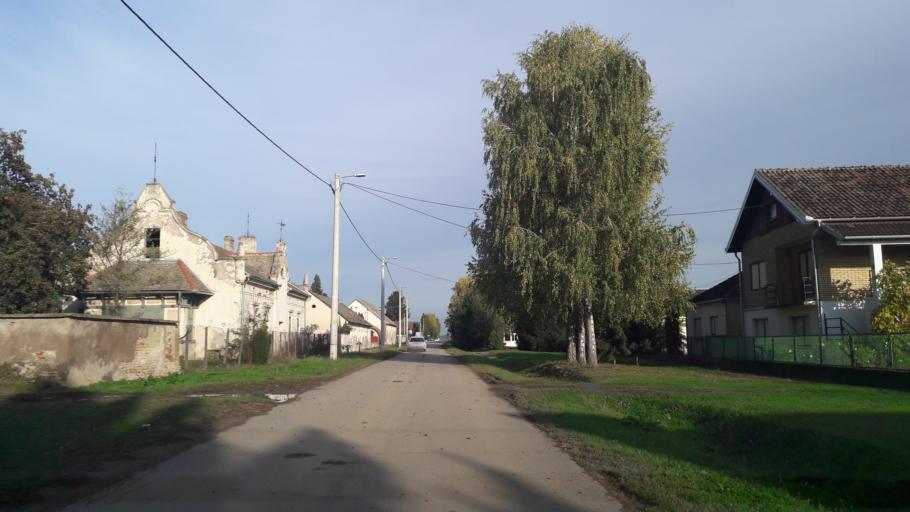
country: HR
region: Osjecko-Baranjska
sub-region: Grad Osijek
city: Karanac
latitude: 45.7621
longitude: 18.6832
